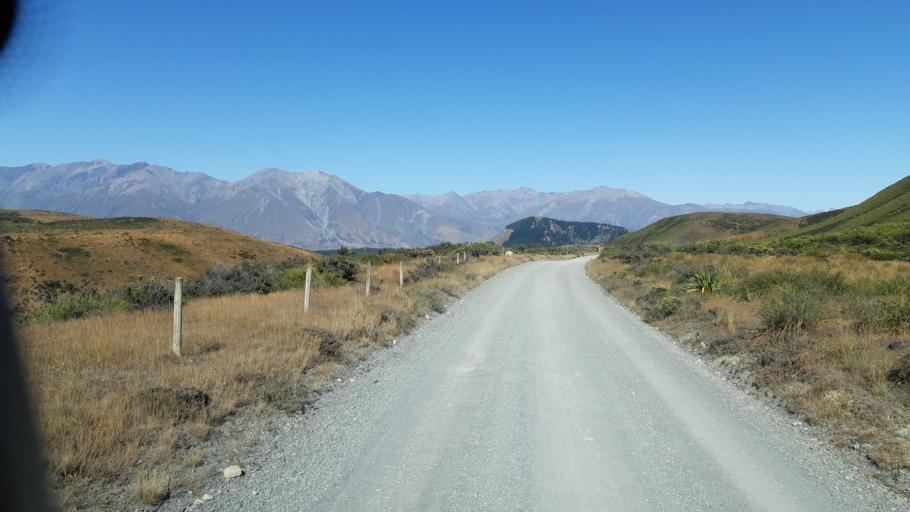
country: NZ
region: Canterbury
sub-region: Ashburton District
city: Methven
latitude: -43.3352
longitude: 171.6612
